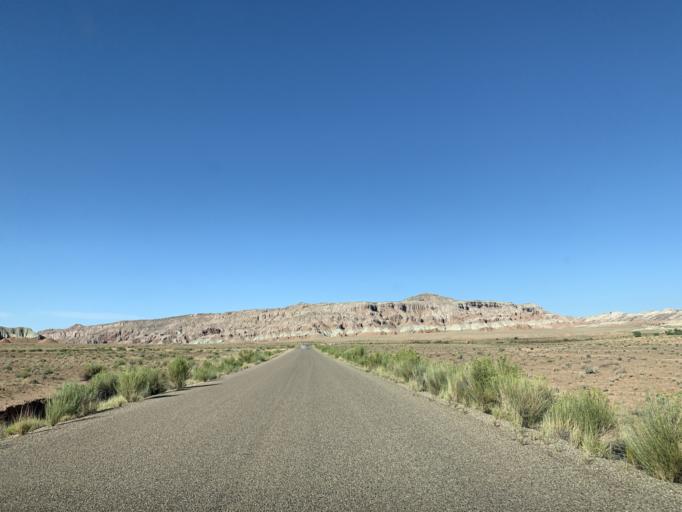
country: US
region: Utah
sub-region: Emery County
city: Ferron
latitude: 38.5771
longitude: -110.7375
